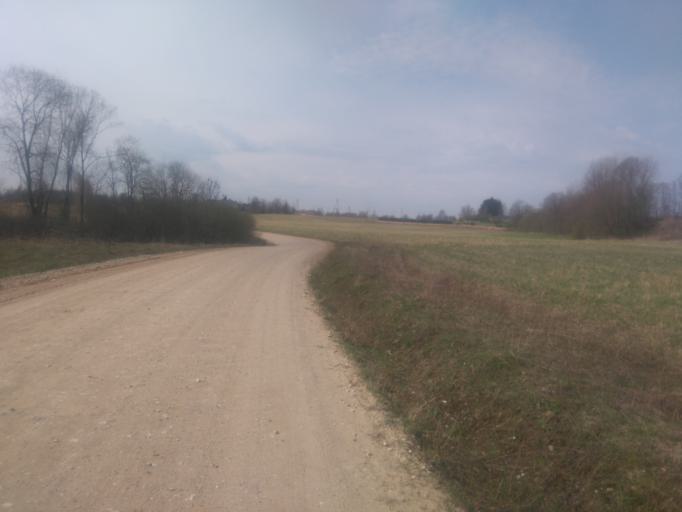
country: LV
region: Vecpiebalga
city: Vecpiebalga
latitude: 57.0232
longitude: 25.8423
